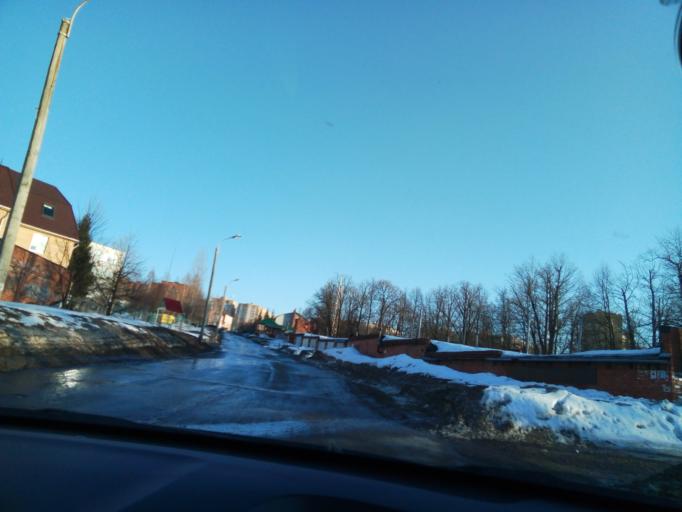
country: RU
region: Chuvashia
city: Novyye Lapsary
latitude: 56.1373
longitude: 47.1550
